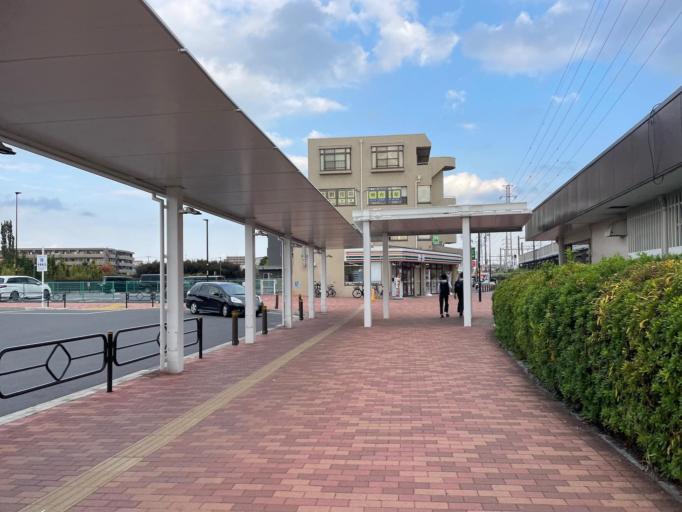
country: JP
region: Tokyo
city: Hino
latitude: 35.7291
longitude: 139.3921
